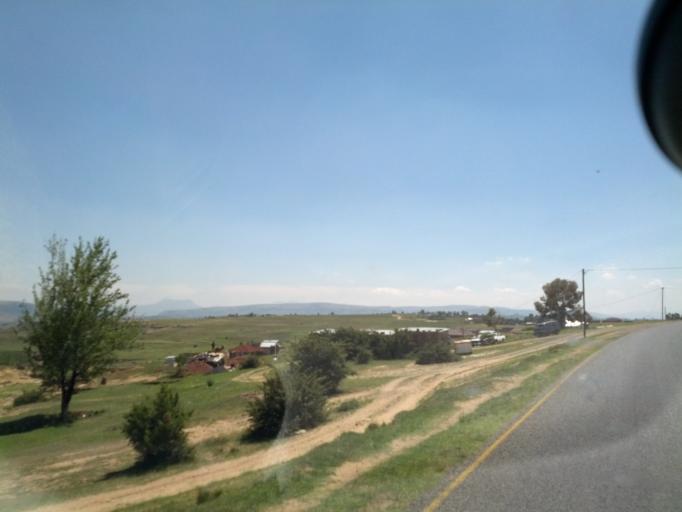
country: LS
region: Butha-Buthe
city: Butha-Buthe
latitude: -28.7829
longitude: 28.2234
